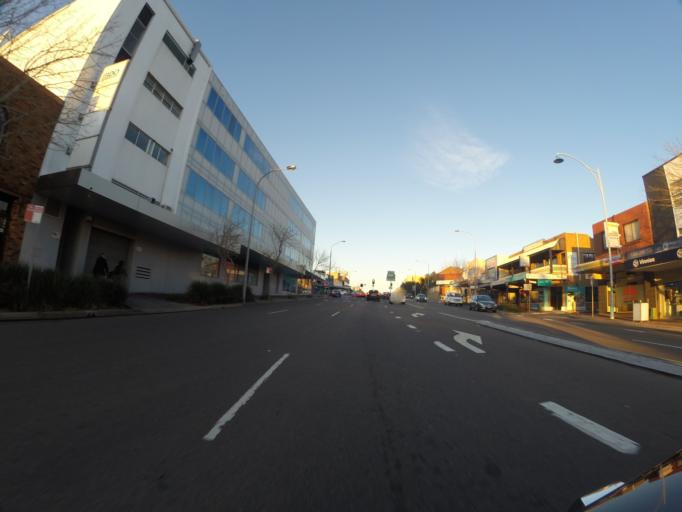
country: AU
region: New South Wales
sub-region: Sutherland Shire
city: Caringbah
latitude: -34.0429
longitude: 151.1219
